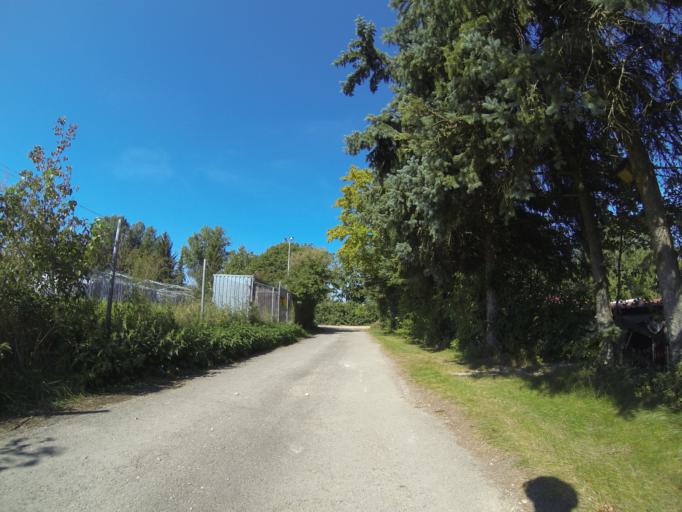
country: DE
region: Baden-Wuerttemberg
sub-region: Tuebingen Region
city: Erbach
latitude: 48.3278
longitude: 9.9102
